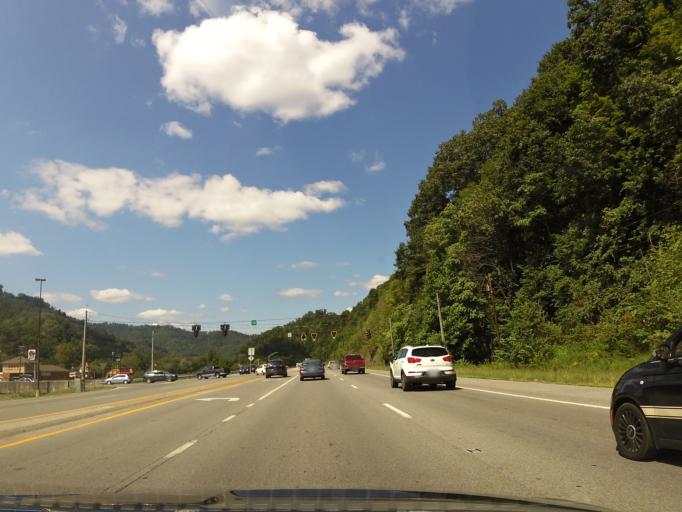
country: US
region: Kentucky
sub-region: Harlan County
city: Harlan
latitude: 36.8190
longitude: -83.3167
